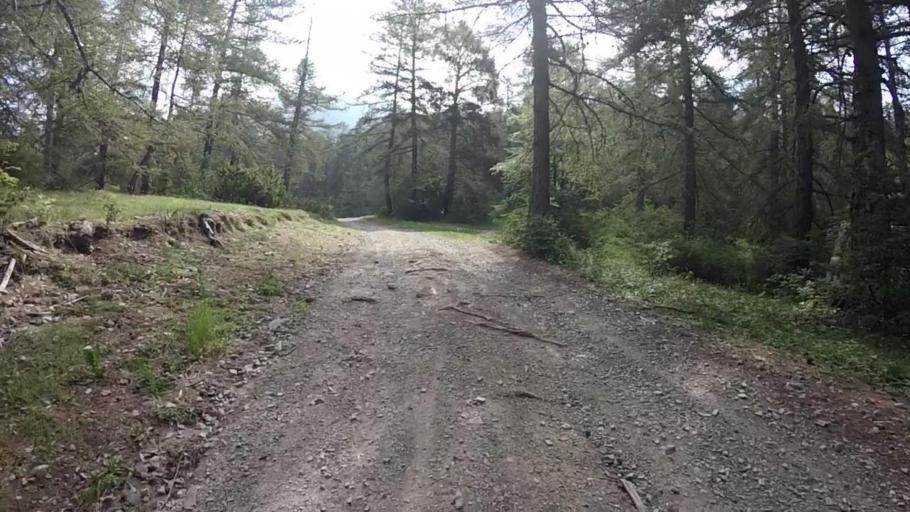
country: FR
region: Provence-Alpes-Cote d'Azur
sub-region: Departement des Alpes-de-Haute-Provence
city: Seyne-les-Alpes
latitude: 44.4032
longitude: 6.3620
